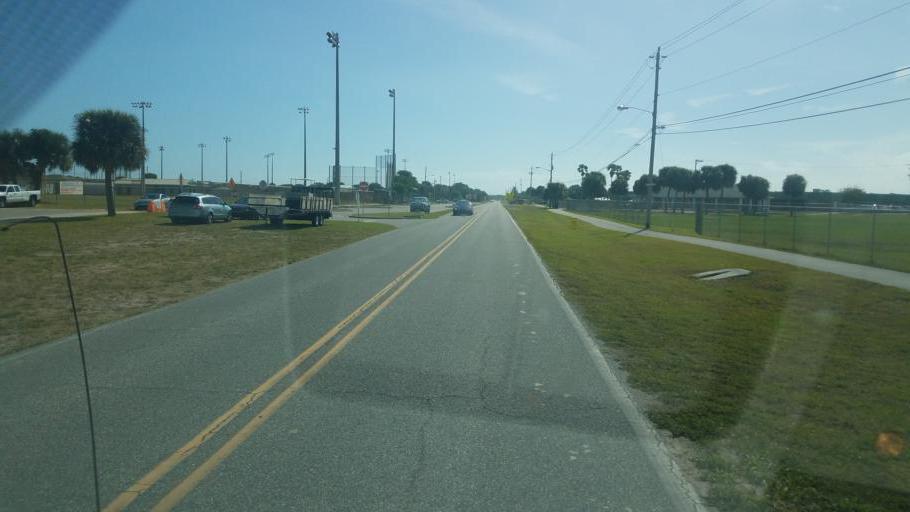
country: US
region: Florida
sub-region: Brevard County
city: Melbourne Beach
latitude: 28.0562
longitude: -80.5564
